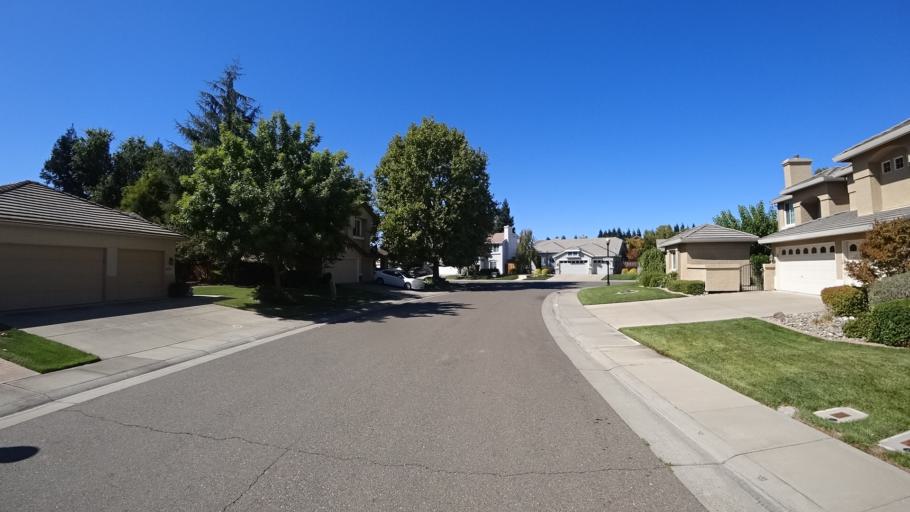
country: US
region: California
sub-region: Sacramento County
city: Laguna
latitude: 38.4132
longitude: -121.4657
